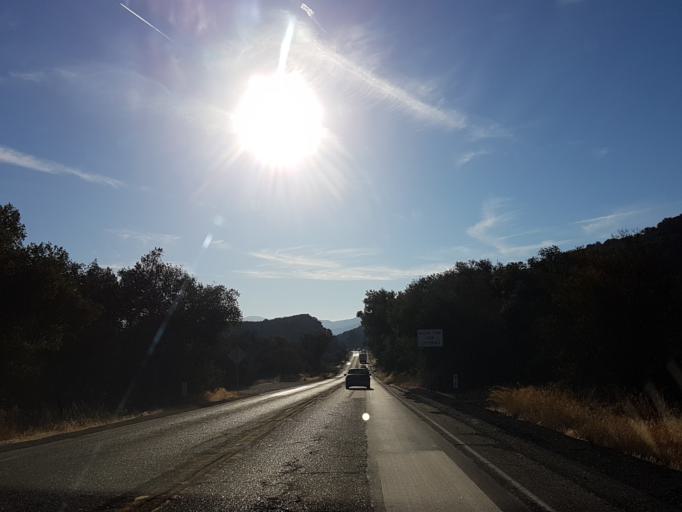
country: US
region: California
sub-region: Santa Barbara County
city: Santa Ynez
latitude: 34.5665
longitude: -119.9406
